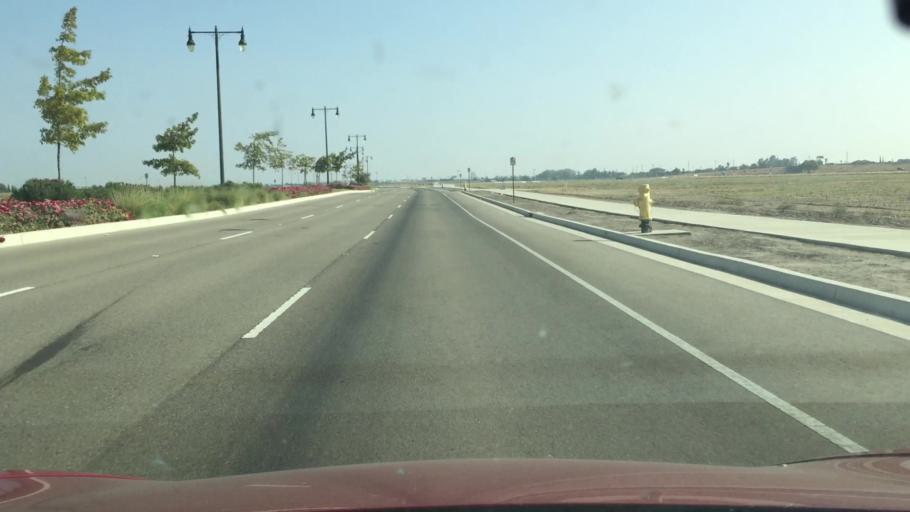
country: US
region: California
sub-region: San Joaquin County
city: Lathrop
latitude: 37.8216
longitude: -121.2976
